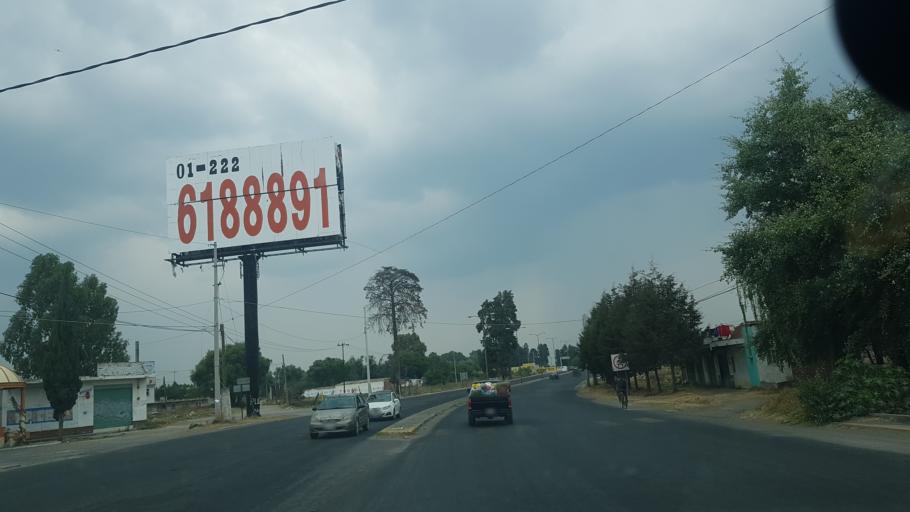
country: MX
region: Puebla
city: Huejotzingo
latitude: 19.1705
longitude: -98.4122
